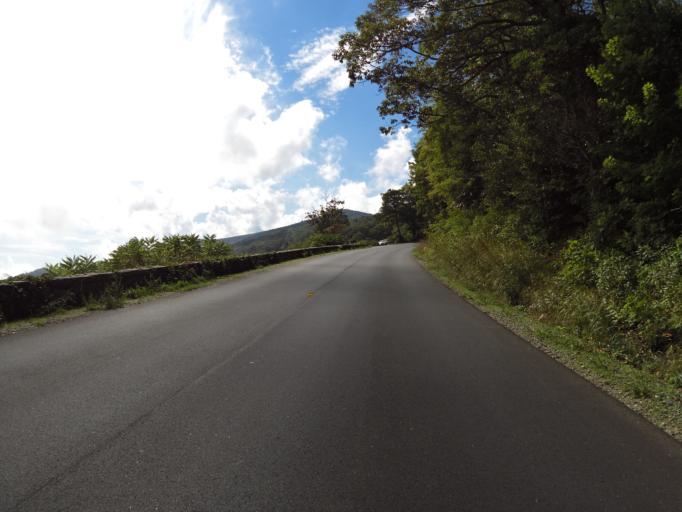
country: US
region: Virginia
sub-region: Page County
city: Luray
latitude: 38.6439
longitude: -78.3085
